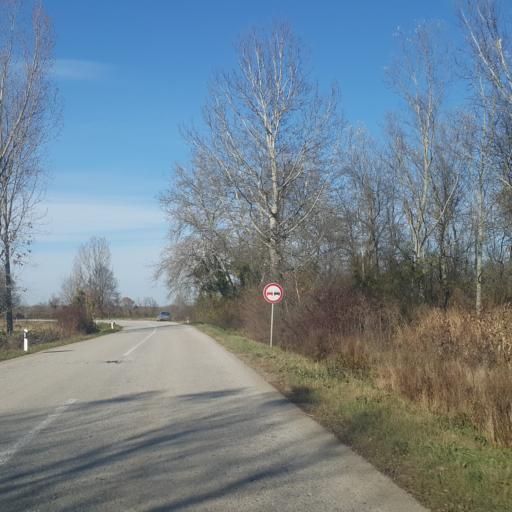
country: RS
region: Central Serbia
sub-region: Sumadijski Okrug
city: Topola
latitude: 44.2519
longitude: 20.8293
